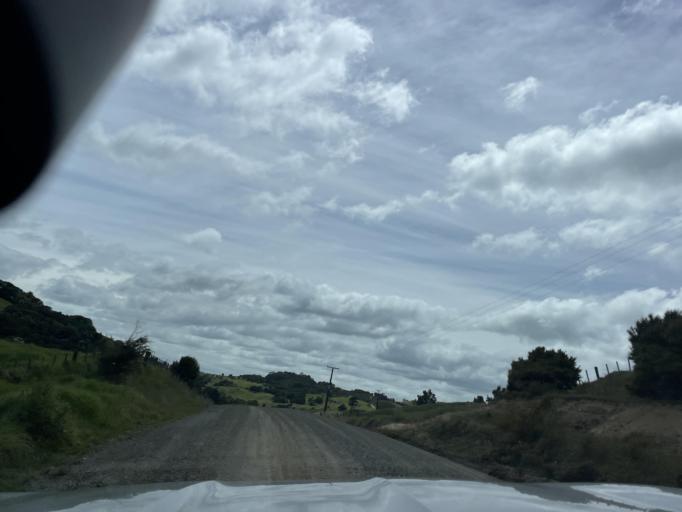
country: NZ
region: Auckland
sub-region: Auckland
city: Wellsford
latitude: -36.1652
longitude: 174.2829
